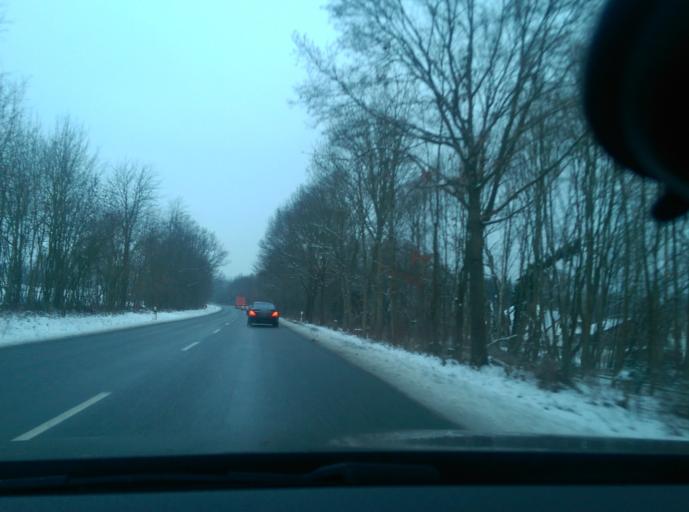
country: DE
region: Hesse
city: Waldkappel
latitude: 51.1570
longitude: 9.8647
